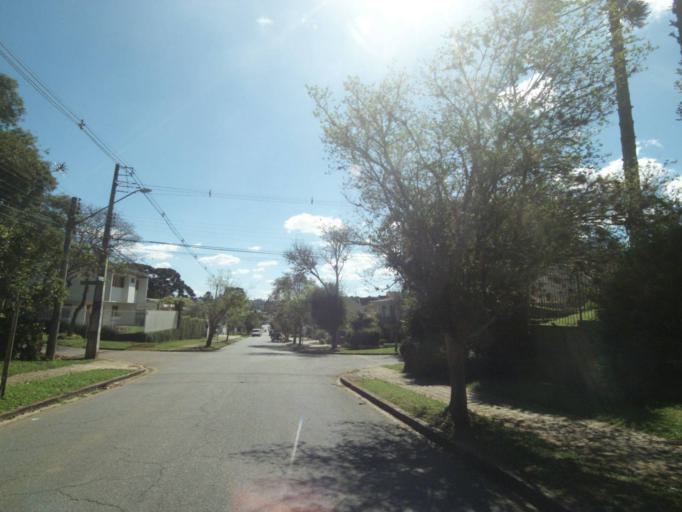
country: BR
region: Parana
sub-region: Curitiba
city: Curitiba
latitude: -25.3987
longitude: -49.2671
